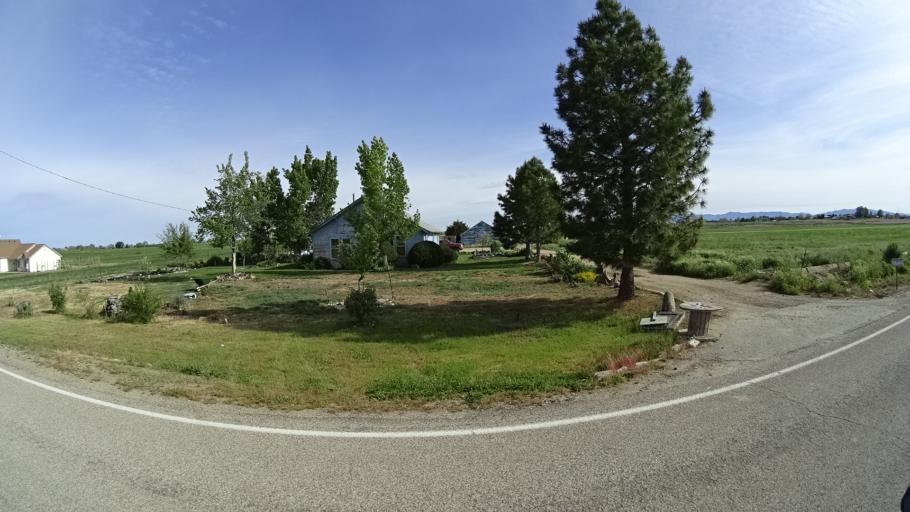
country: US
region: Idaho
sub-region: Ada County
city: Kuna
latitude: 43.4735
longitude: -116.3433
